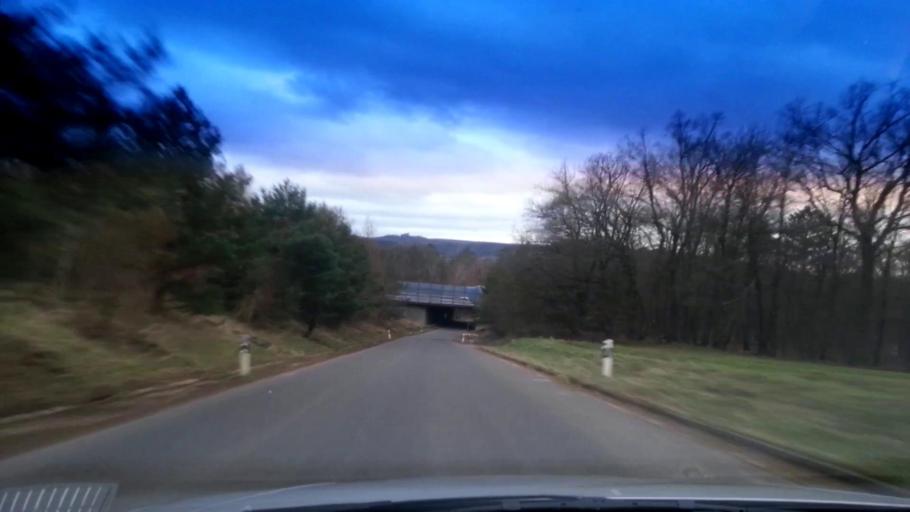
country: DE
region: Bavaria
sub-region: Upper Franconia
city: Schesslitz
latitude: 49.9837
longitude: 11.0625
